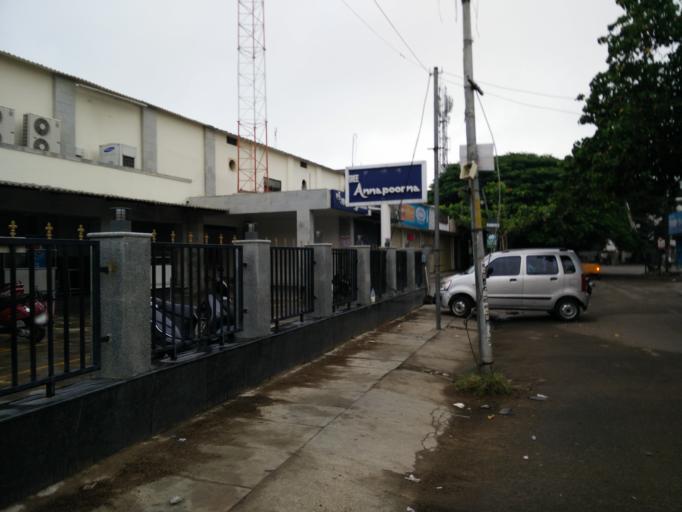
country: IN
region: Tamil Nadu
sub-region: Coimbatore
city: Coimbatore
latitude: 11.0254
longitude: 76.9427
